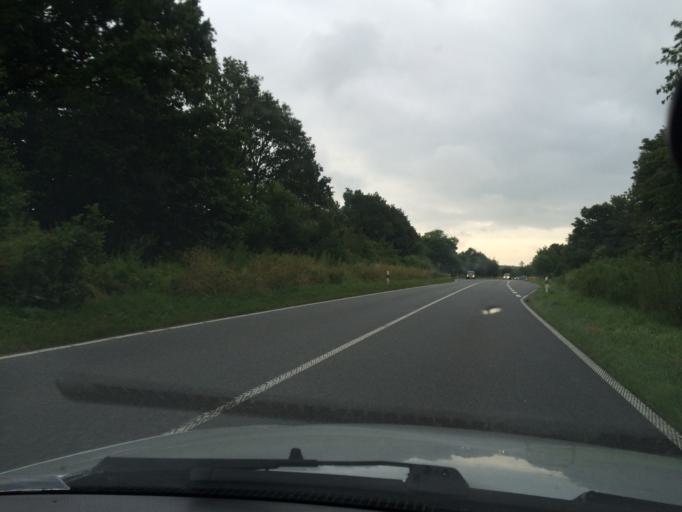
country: DE
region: Schleswig-Holstein
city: Sieverstedt
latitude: 54.6426
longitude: 9.4607
